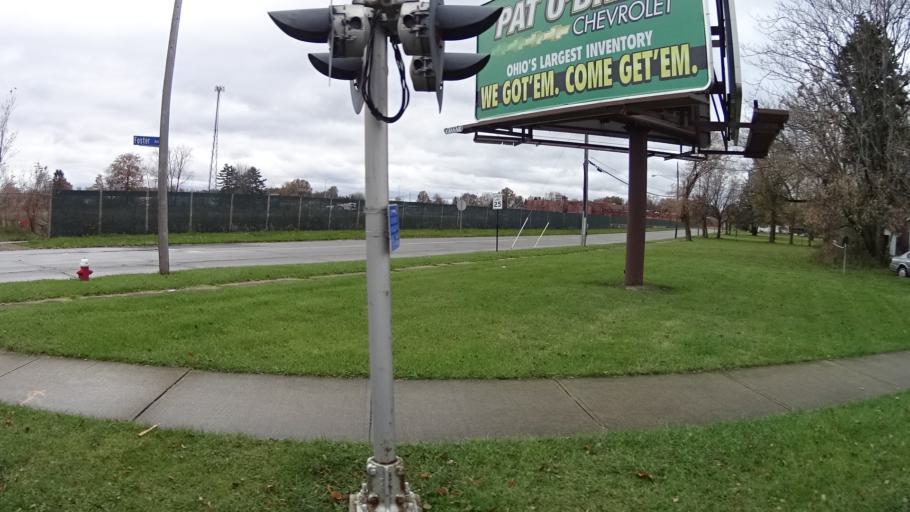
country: US
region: Ohio
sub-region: Lorain County
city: Elyria
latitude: 41.3786
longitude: -82.1223
